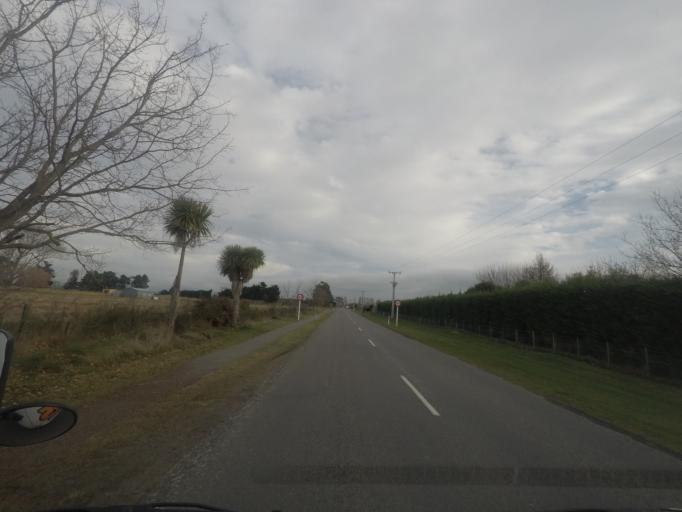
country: NZ
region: Canterbury
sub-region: Waimakariri District
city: Woodend
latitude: -43.2880
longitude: 172.7072
